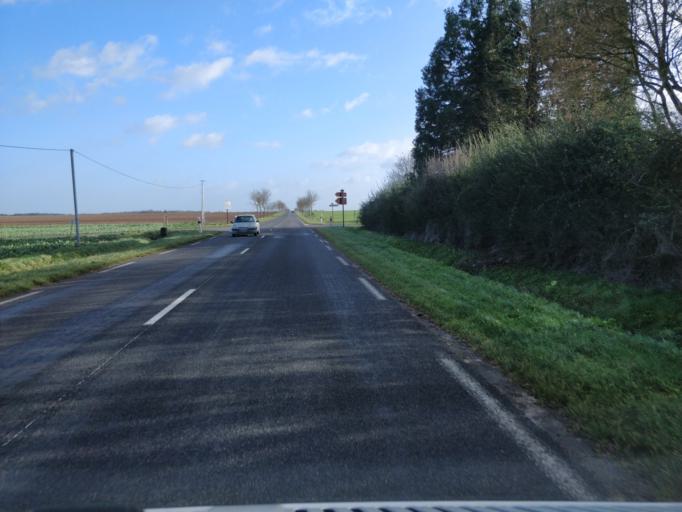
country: FR
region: Ile-de-France
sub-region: Departement de Seine-et-Marne
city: Lorrez-le-Bocage-Preaux
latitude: 48.2110
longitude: 2.9409
